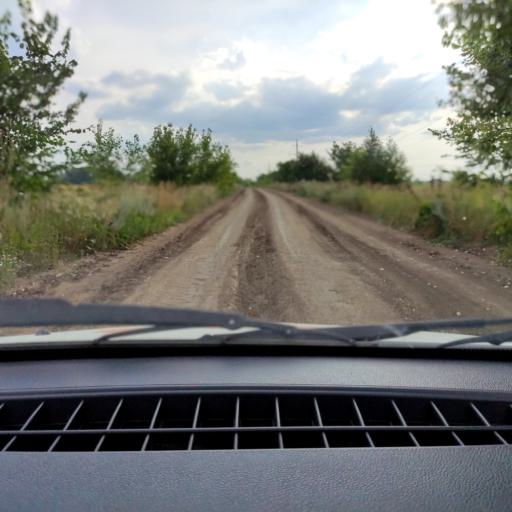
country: RU
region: Bashkortostan
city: Blagoveshchensk
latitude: 54.9262
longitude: 55.9461
